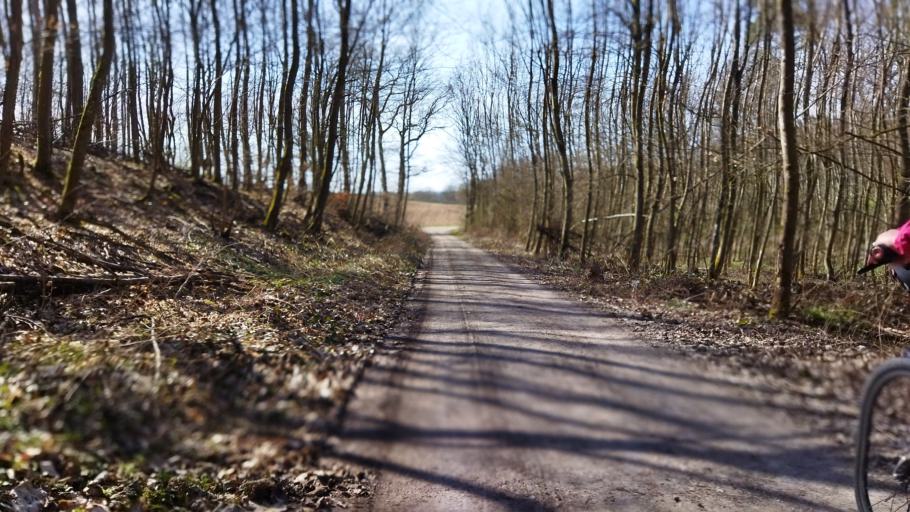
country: DE
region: Baden-Wuerttemberg
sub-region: Regierungsbezirk Stuttgart
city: Eppingen
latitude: 49.1229
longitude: 8.9264
